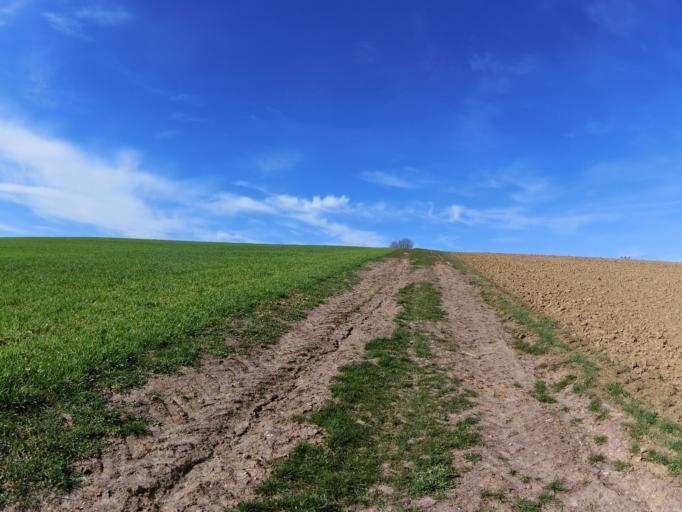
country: DE
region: Bavaria
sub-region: Regierungsbezirk Unterfranken
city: Biebelried
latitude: 49.7962
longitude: 10.0992
